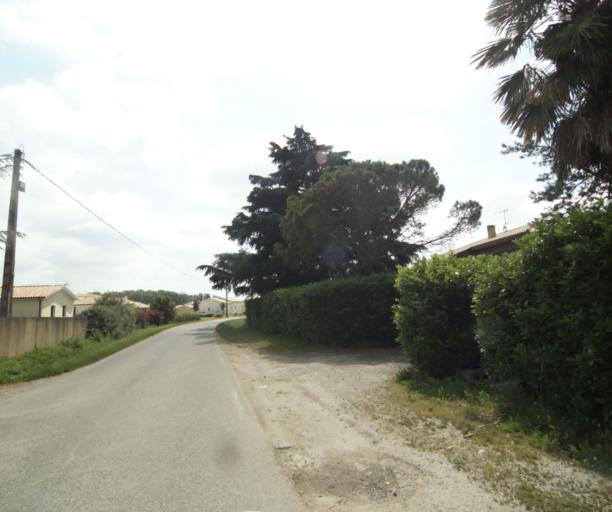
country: FR
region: Midi-Pyrenees
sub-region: Departement du Tarn-et-Garonne
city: Albias
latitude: 44.0676
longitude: 1.4130
